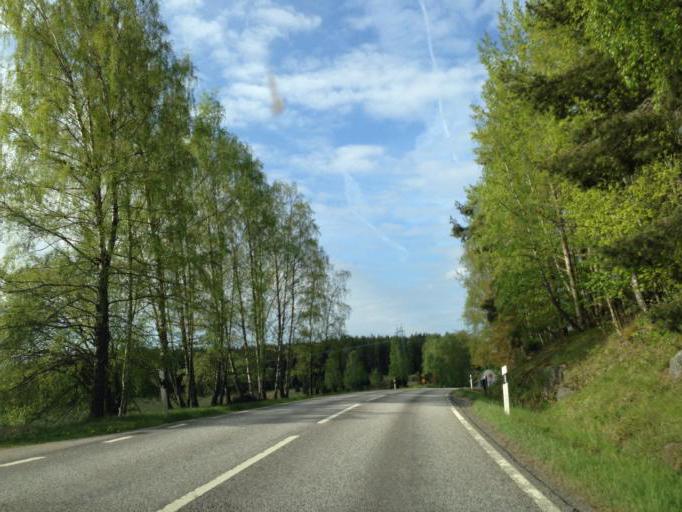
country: SE
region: Soedermanland
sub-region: Nykopings Kommun
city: Stigtomta
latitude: 58.9516
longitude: 16.8545
